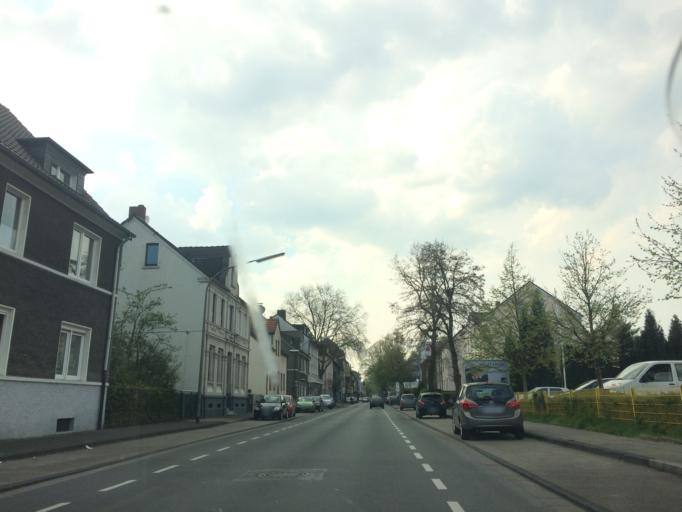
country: DE
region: North Rhine-Westphalia
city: Herten
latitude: 51.5779
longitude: 7.1118
